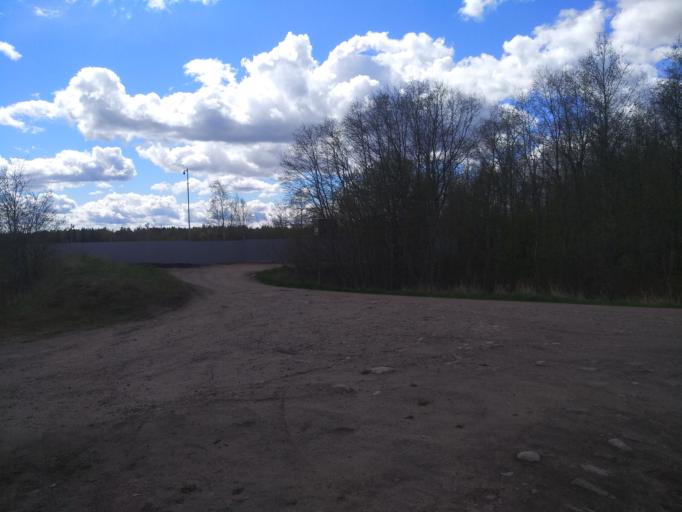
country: RU
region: Leningrad
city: Garbolovo
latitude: 60.5733
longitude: 30.6775
